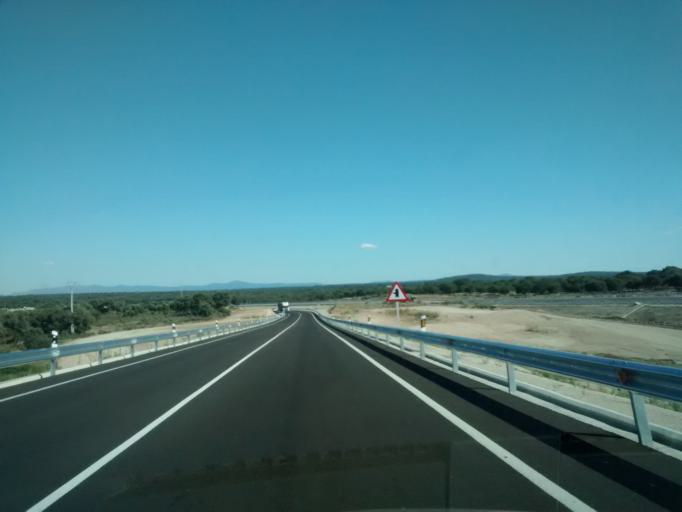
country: ES
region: Castille and Leon
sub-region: Provincia de Salamanca
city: Fuentes de Onoro
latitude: 40.5909
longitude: -6.7815
